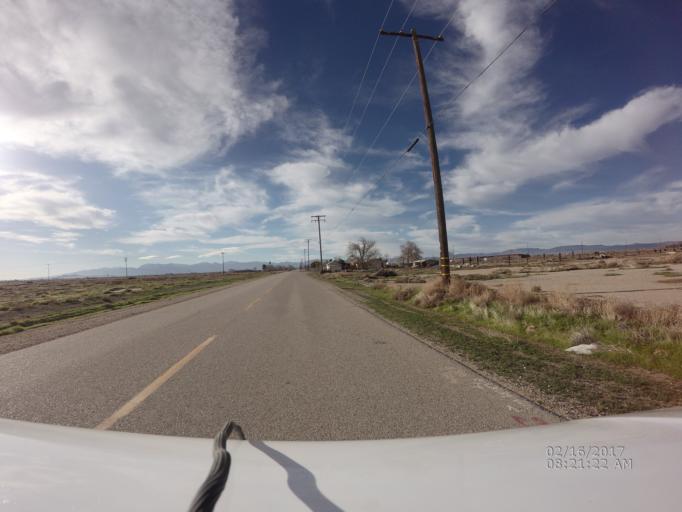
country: US
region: California
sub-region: Los Angeles County
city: Lancaster
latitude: 34.7357
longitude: -118.0053
